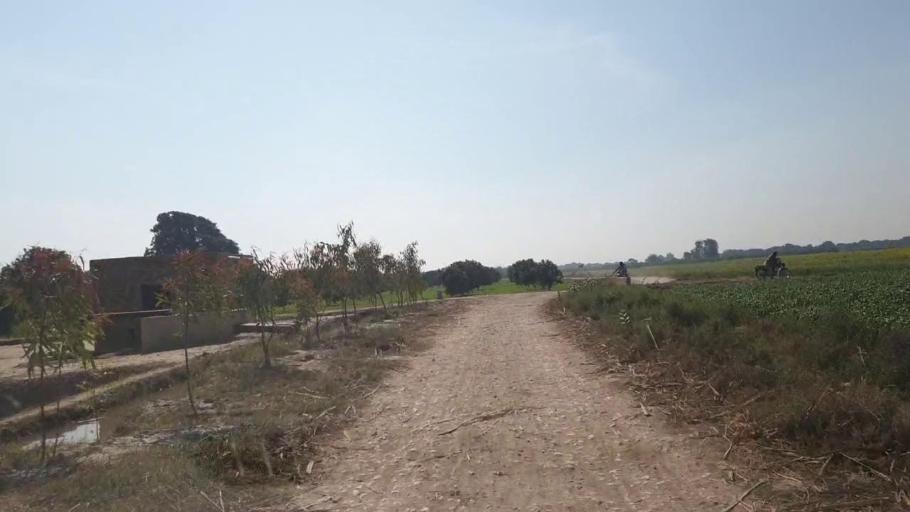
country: PK
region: Sindh
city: Tando Allahyar
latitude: 25.3972
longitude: 68.7817
